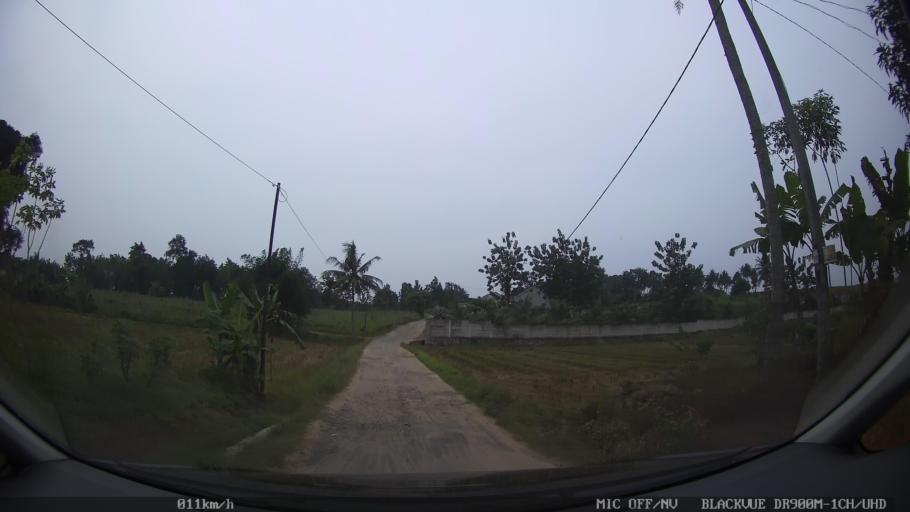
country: ID
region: Lampung
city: Panjang
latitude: -5.4123
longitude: 105.3570
